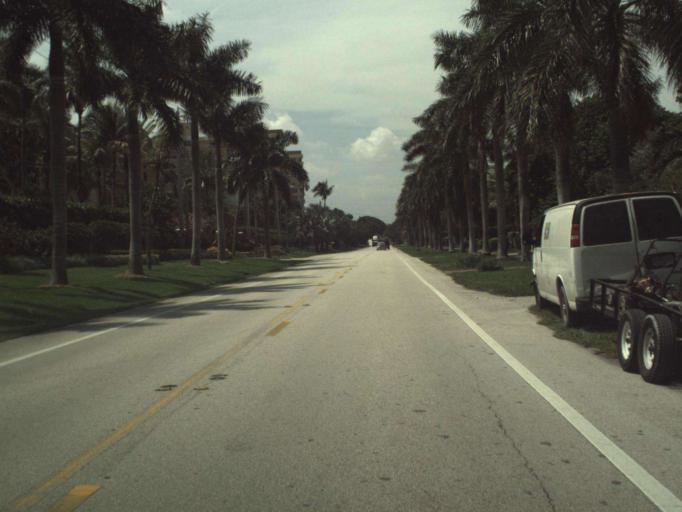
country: US
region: Florida
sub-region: Palm Beach County
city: Highland Beach
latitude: 26.3988
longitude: -80.0660
